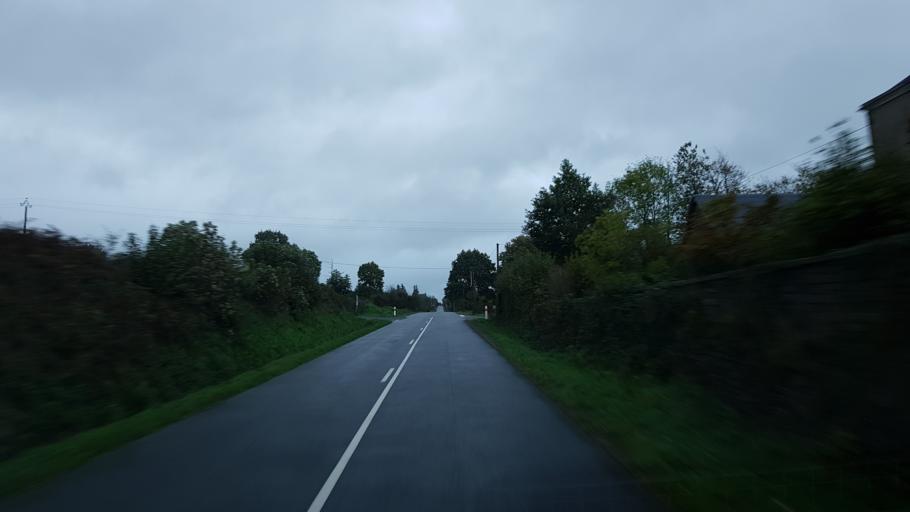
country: FR
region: Pays de la Loire
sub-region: Departement de la Mayenne
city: Juvigne
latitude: 48.2004
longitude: -1.0698
